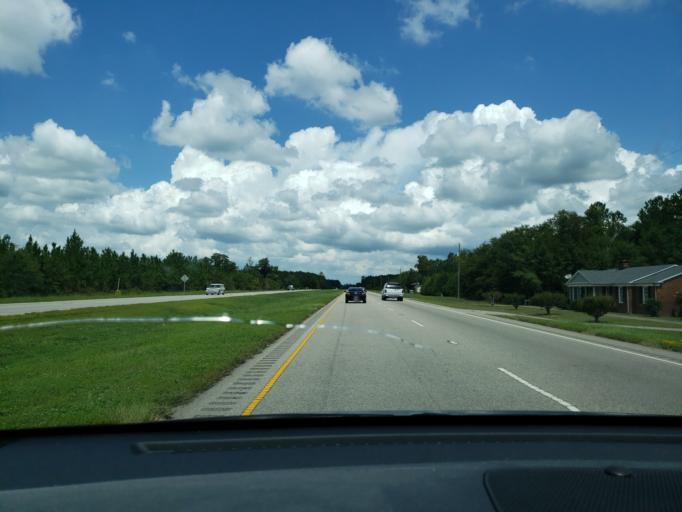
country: US
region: North Carolina
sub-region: Bladen County
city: Elizabethtown
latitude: 34.6849
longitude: -78.7411
